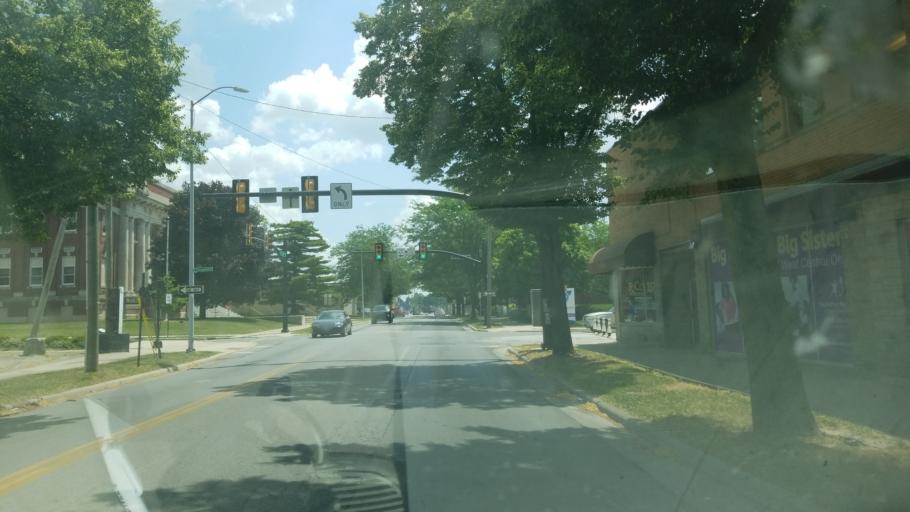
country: US
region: Ohio
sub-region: Allen County
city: Lima
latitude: 40.7372
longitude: -84.1073
